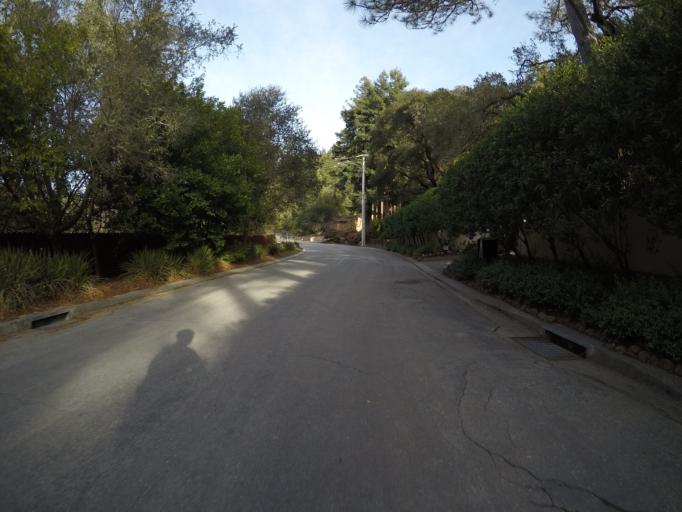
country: US
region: California
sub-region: Santa Cruz County
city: Mount Hermon
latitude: 37.0323
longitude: -122.0369
